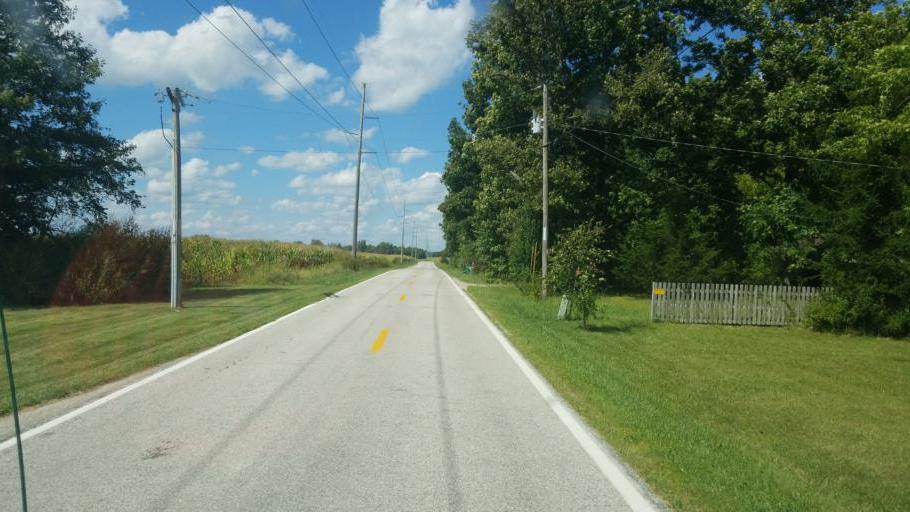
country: US
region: Ohio
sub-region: Marion County
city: Prospect
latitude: 40.3276
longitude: -83.2037
